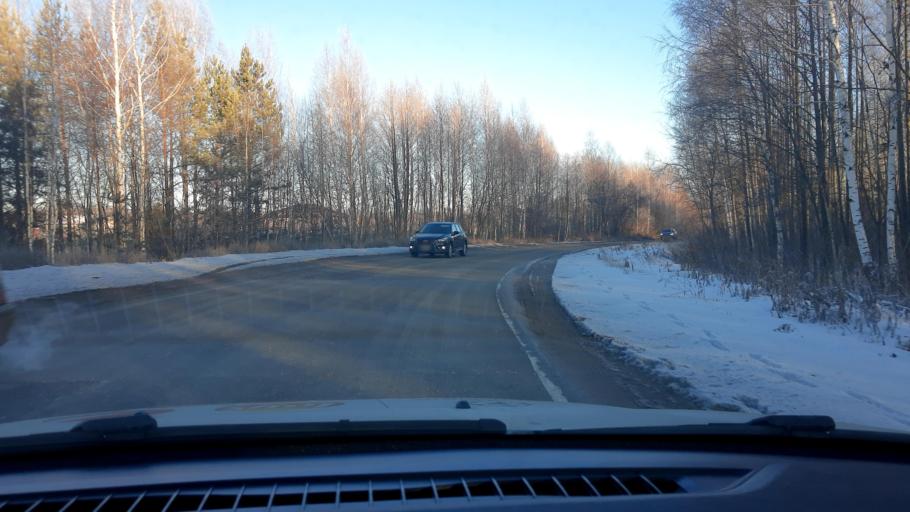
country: RU
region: Nizjnij Novgorod
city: Novosmolinskiy
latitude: 56.2927
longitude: 43.0229
